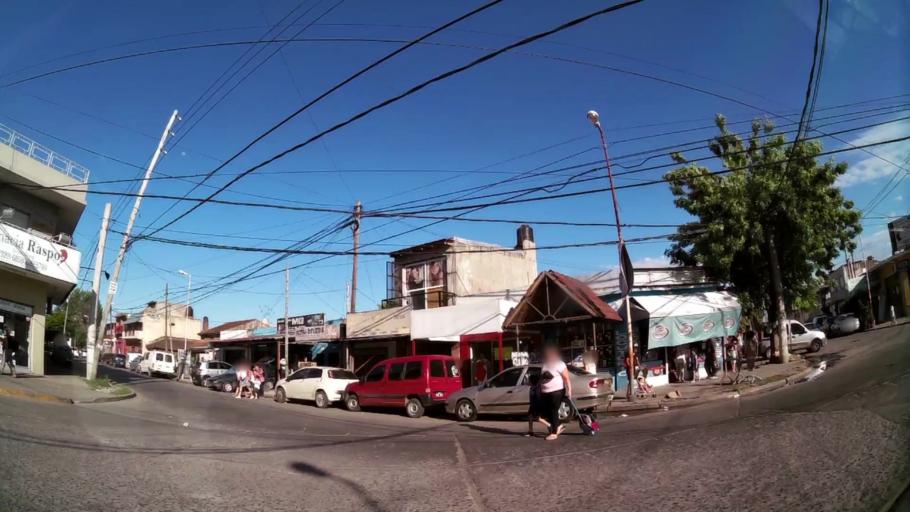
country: AR
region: Buenos Aires
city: Santa Catalina - Dique Lujan
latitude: -34.4906
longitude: -58.7270
